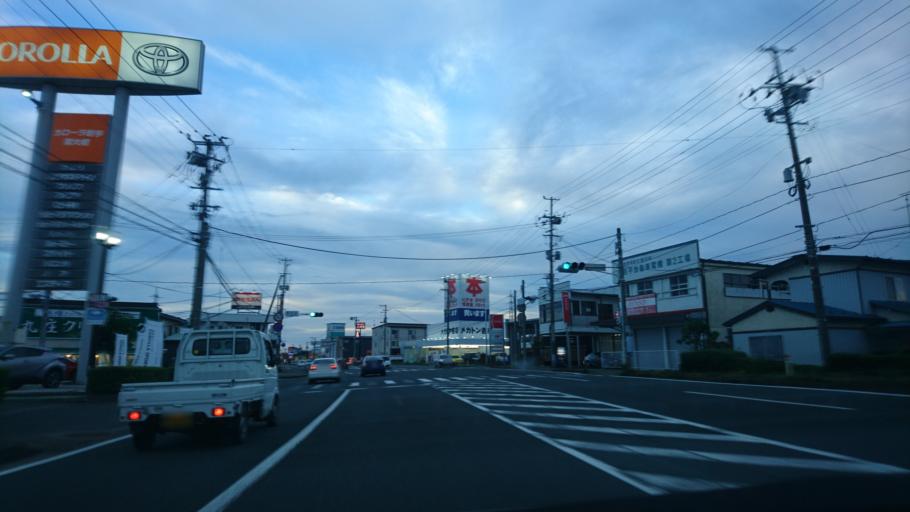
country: JP
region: Iwate
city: Morioka-shi
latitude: 39.6820
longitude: 141.1561
